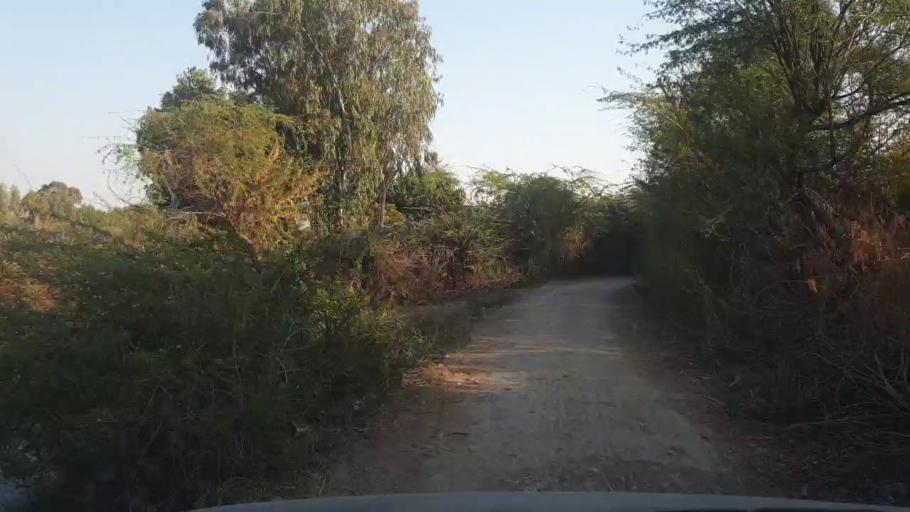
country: PK
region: Sindh
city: Chambar
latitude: 25.2575
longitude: 68.8978
